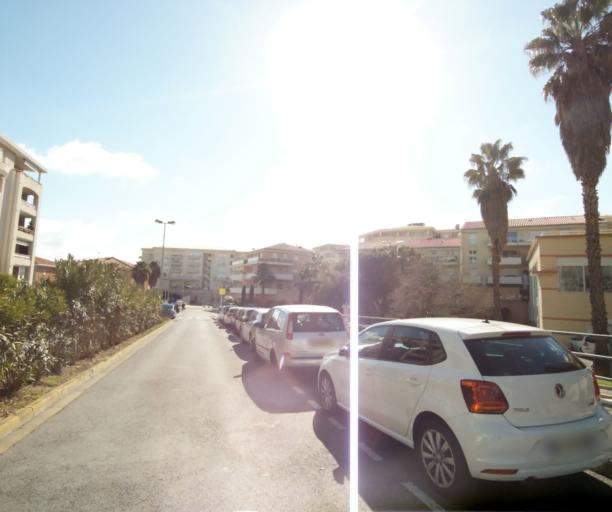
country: FR
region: Provence-Alpes-Cote d'Azur
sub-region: Departement des Alpes-Maritimes
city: Vallauris
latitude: 43.5734
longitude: 7.0910
